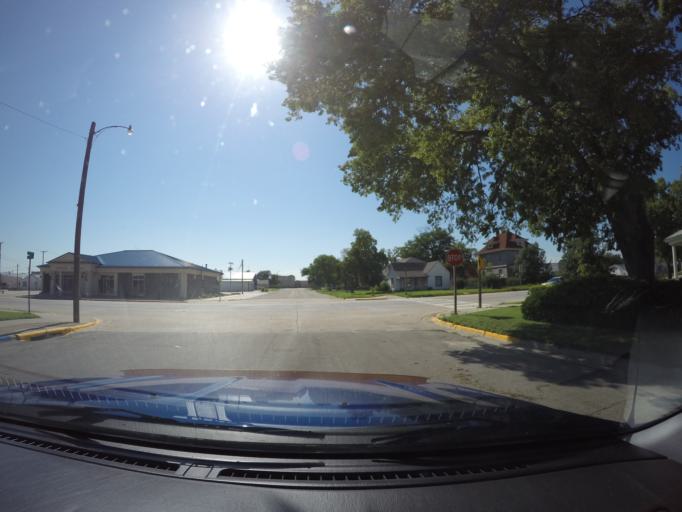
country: US
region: Kansas
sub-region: Rooks County
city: Stockton
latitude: 39.4378
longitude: -99.2749
